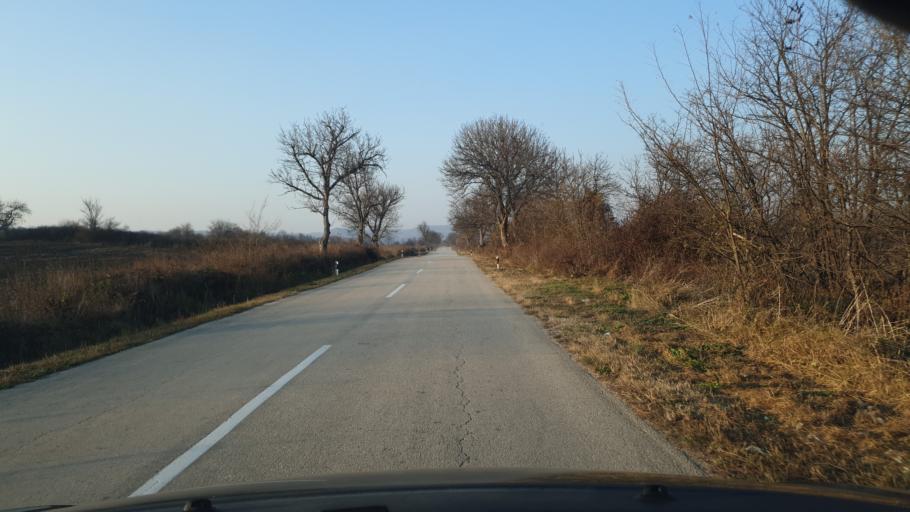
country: RS
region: Central Serbia
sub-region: Zajecarski Okrug
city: Zajecar
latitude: 43.9836
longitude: 22.2878
